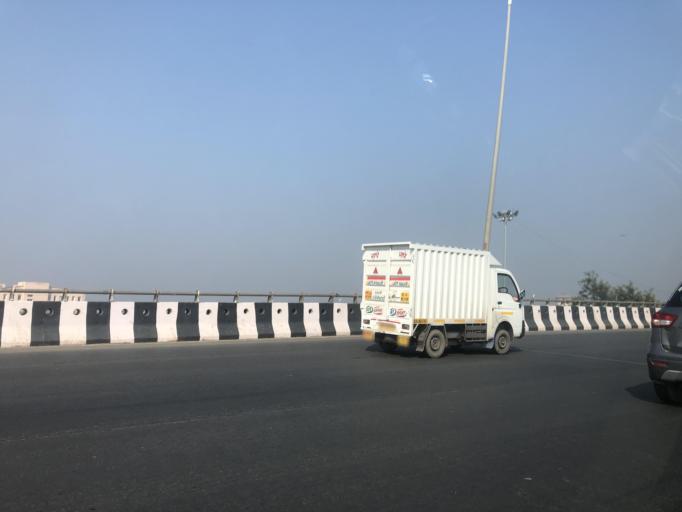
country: IN
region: Haryana
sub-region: Gurgaon
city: Gurgaon
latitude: 28.5430
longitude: 77.1183
